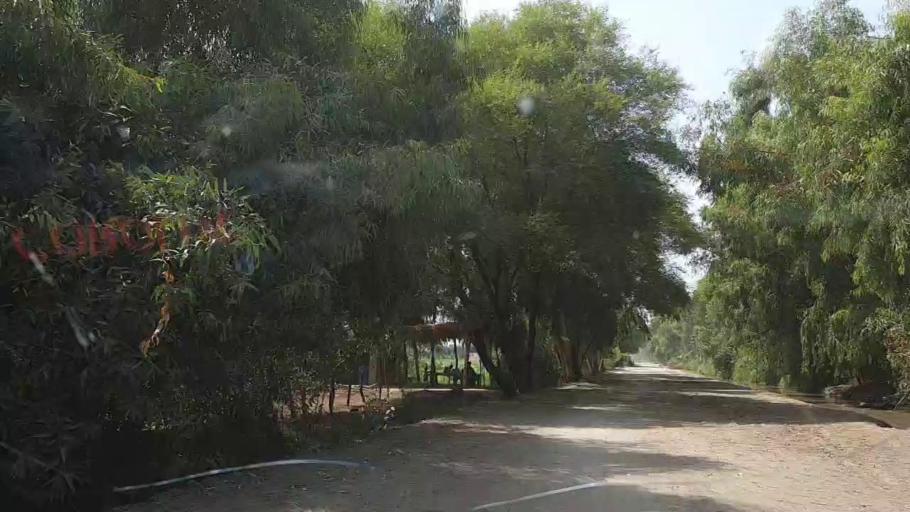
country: PK
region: Sindh
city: Ghotki
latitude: 28.0895
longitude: 69.3339
